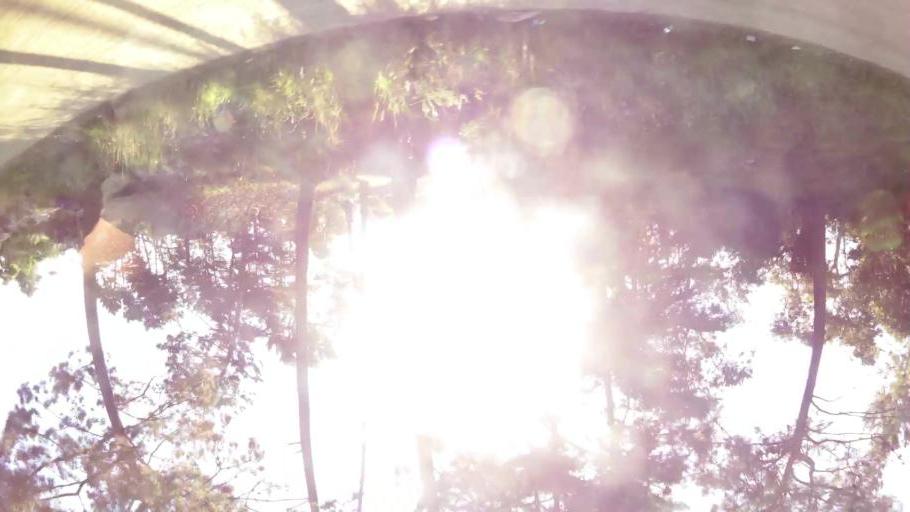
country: UY
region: Canelones
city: Empalme Olmos
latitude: -34.7718
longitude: -55.8573
